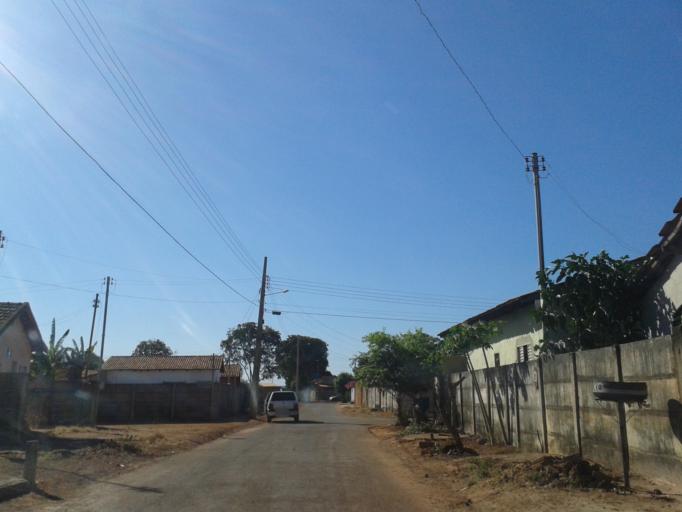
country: BR
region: Goias
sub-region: Sao Miguel Do Araguaia
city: Sao Miguel do Araguaia
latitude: -13.2835
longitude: -50.1766
